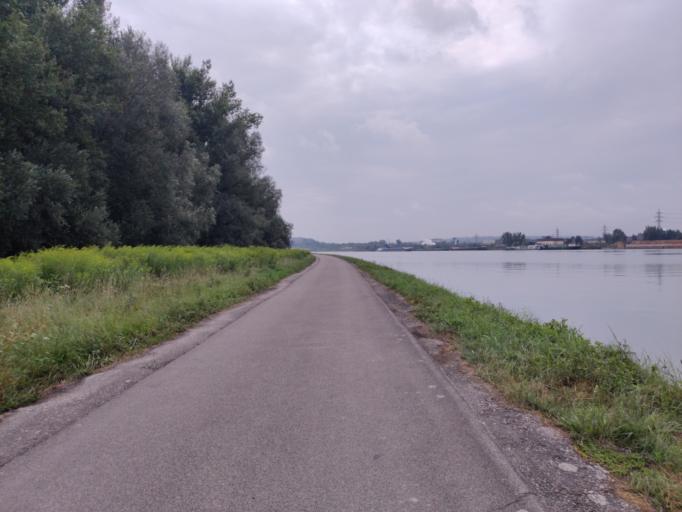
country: AT
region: Upper Austria
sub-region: Politischer Bezirk Urfahr-Umgebung
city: Steyregg
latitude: 48.2853
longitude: 14.3462
